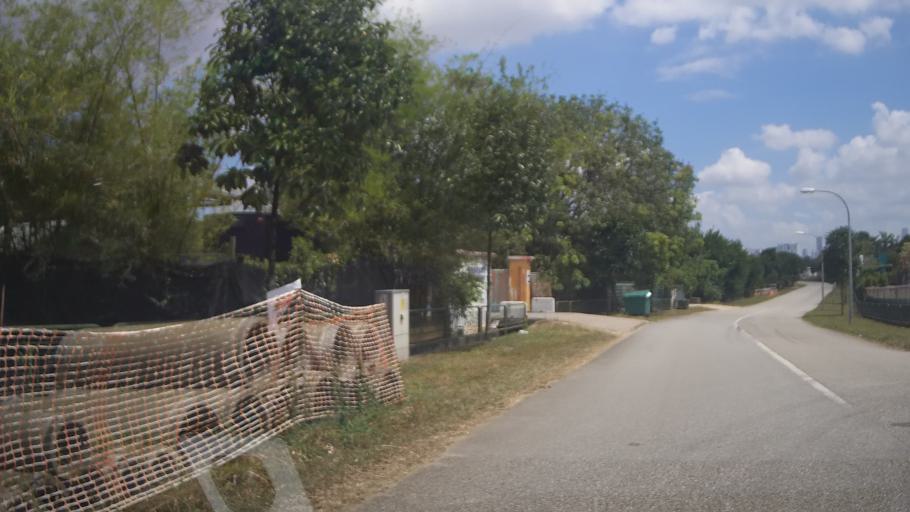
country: MY
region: Johor
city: Johor Bahru
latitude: 1.4394
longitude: 103.7270
